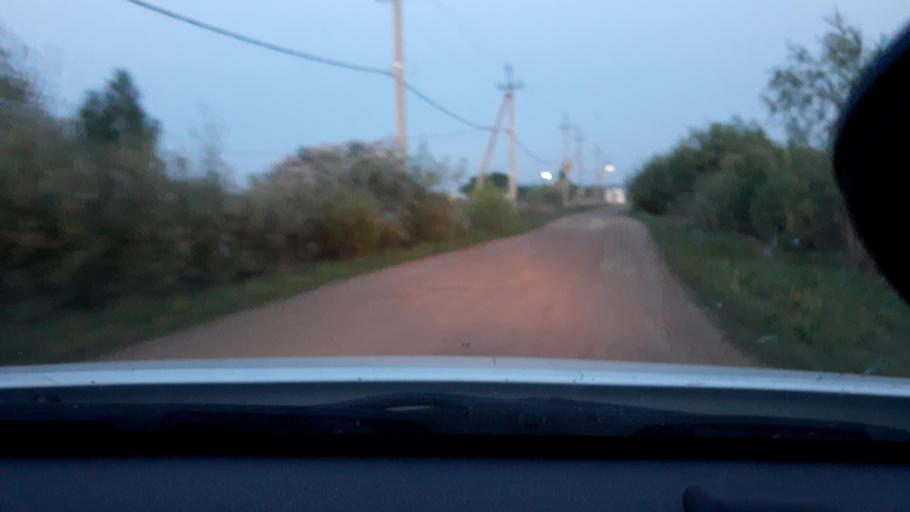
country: RU
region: Bashkortostan
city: Avdon
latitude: 54.5279
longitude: 55.8210
